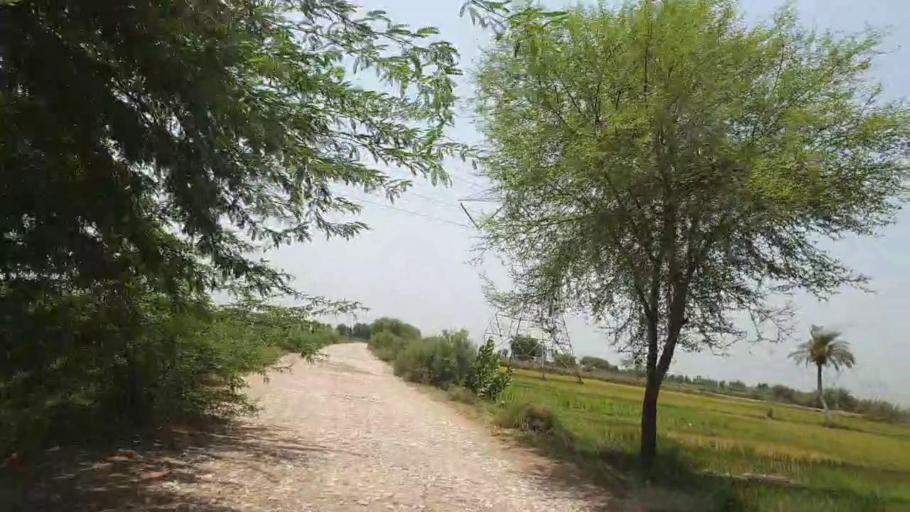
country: PK
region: Sindh
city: Shikarpur
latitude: 27.8891
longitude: 68.6301
